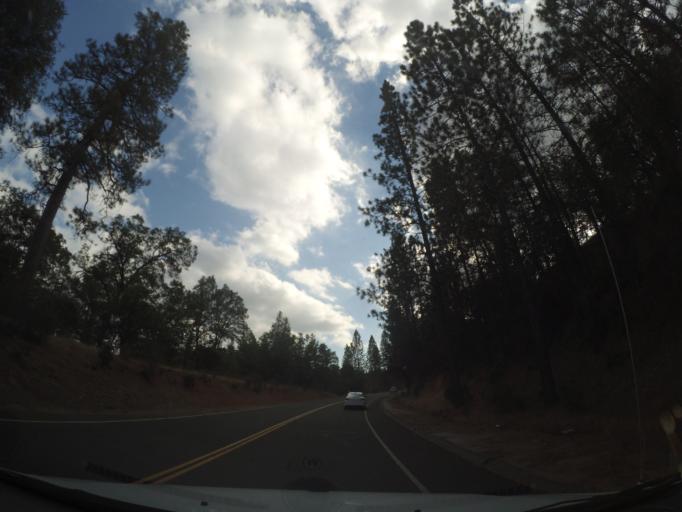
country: US
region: California
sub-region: Mariposa County
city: Midpines
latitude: 37.5403
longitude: -119.9176
